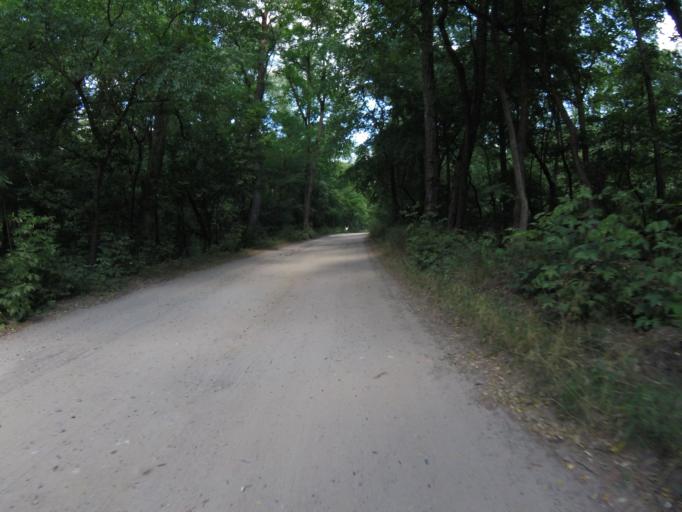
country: DE
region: Brandenburg
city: Bestensee
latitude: 52.2690
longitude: 13.6577
